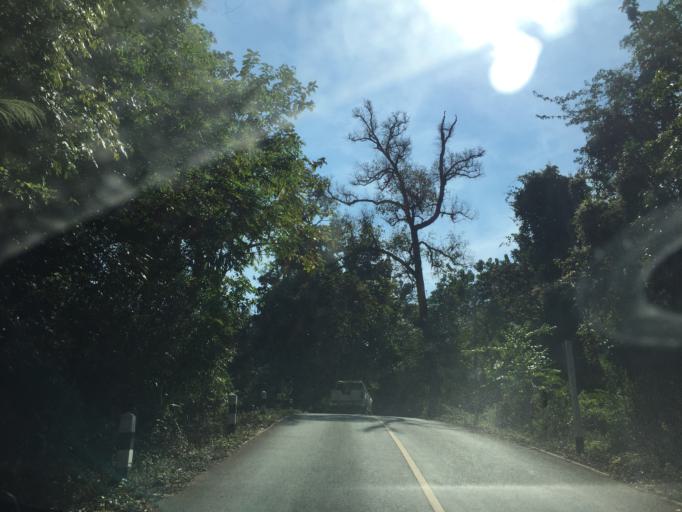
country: TH
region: Chiang Mai
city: Samoeng
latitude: 18.9525
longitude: 98.7933
